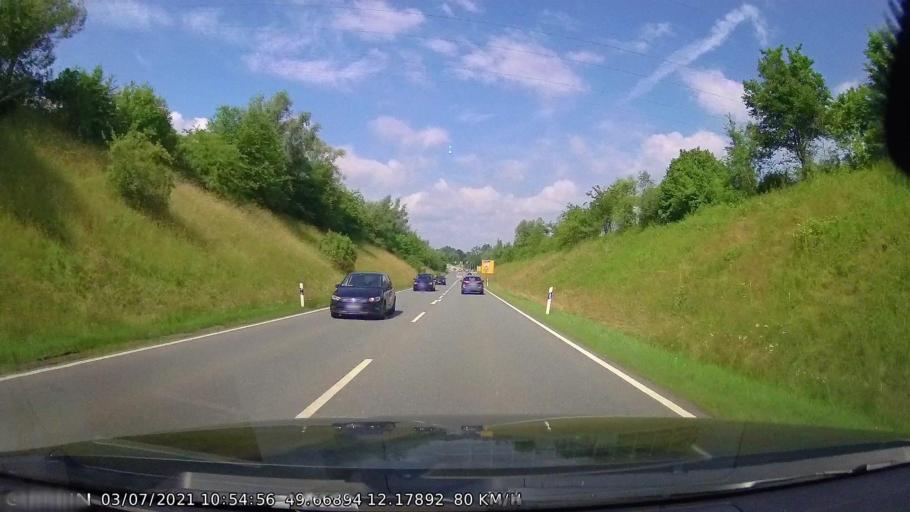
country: DE
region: Bavaria
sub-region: Upper Palatinate
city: Schirmitz
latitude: 49.6690
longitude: 12.1786
